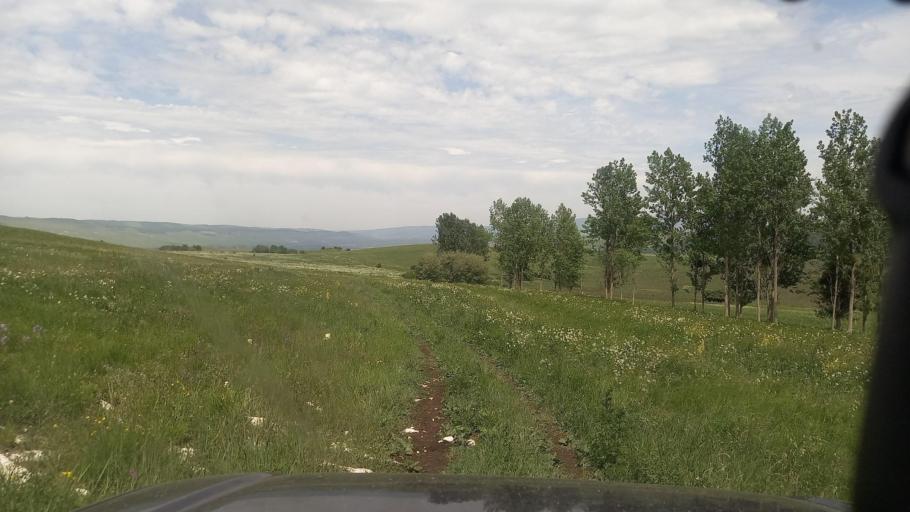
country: RU
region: Karachayevo-Cherkesiya
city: Pregradnaya
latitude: 44.0688
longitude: 41.3132
